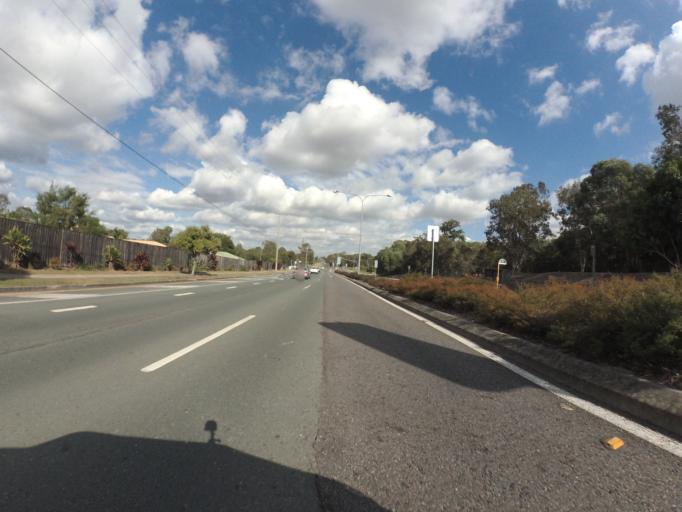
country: AU
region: Queensland
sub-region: Brisbane
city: Wynnum West
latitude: -27.4607
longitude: 153.1490
